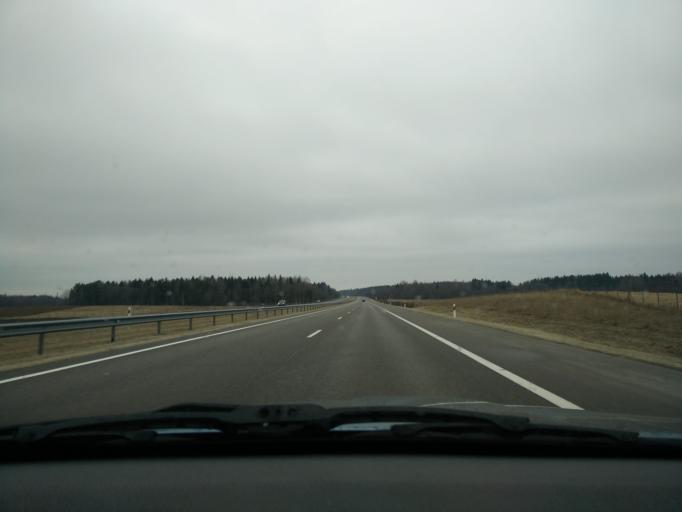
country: LT
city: Silale
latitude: 55.6023
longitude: 22.1053
